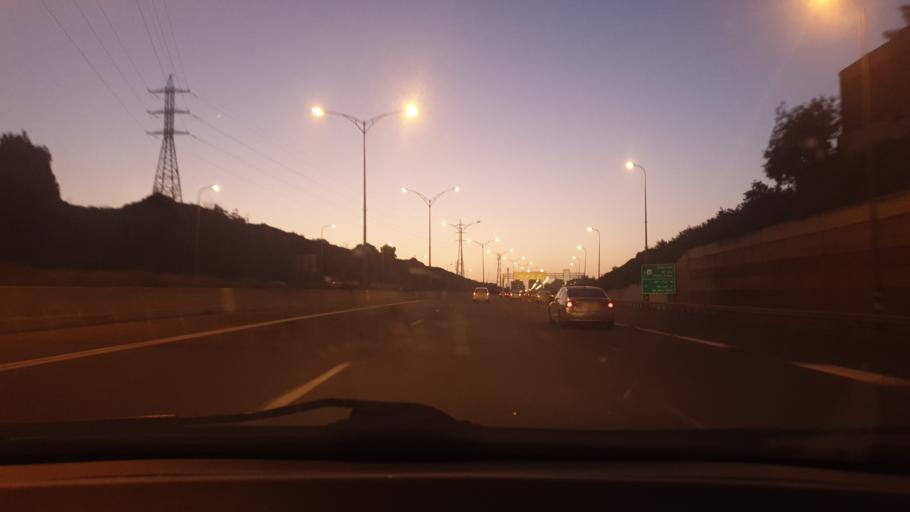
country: IL
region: Central District
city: Ganne Tiqwa
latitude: 32.0706
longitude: 34.8809
